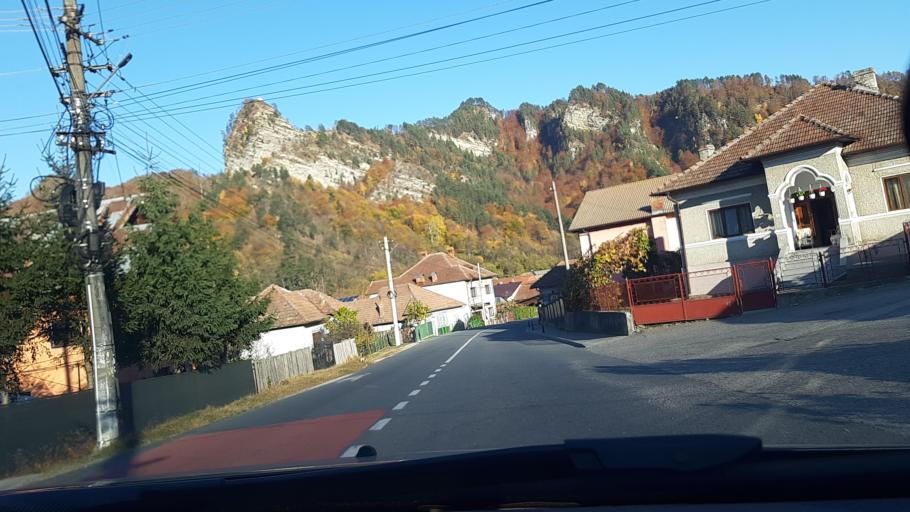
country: RO
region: Valcea
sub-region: Comuna Brezoi
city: Brezoi
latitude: 45.3443
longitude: 24.2392
